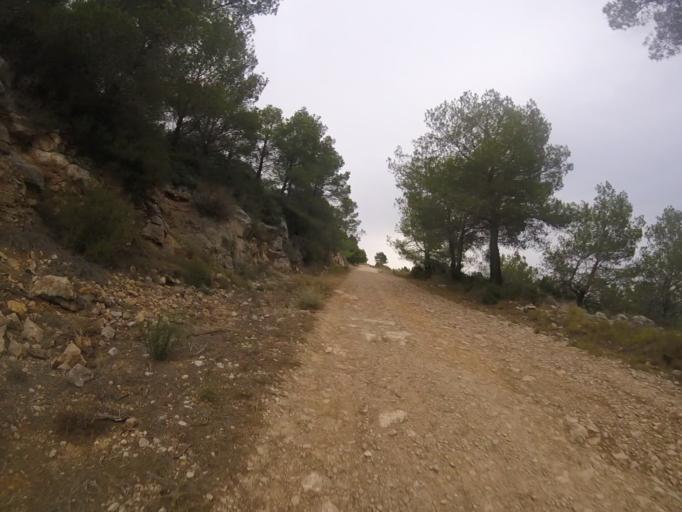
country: ES
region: Valencia
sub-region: Provincia de Castello
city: Alcoceber
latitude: 40.2768
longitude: 0.2811
